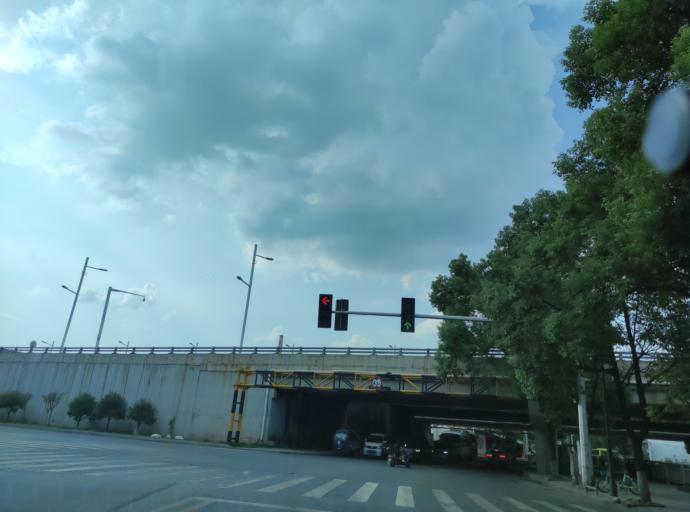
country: CN
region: Jiangxi Sheng
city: Pingxiang
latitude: 27.6620
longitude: 113.8361
